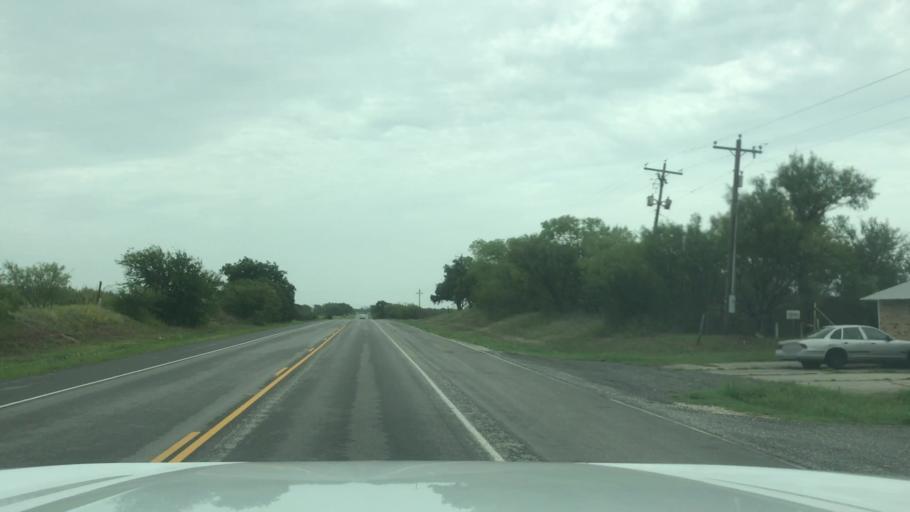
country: US
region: Texas
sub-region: Eastland County
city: Gorman
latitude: 32.2218
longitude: -98.6973
